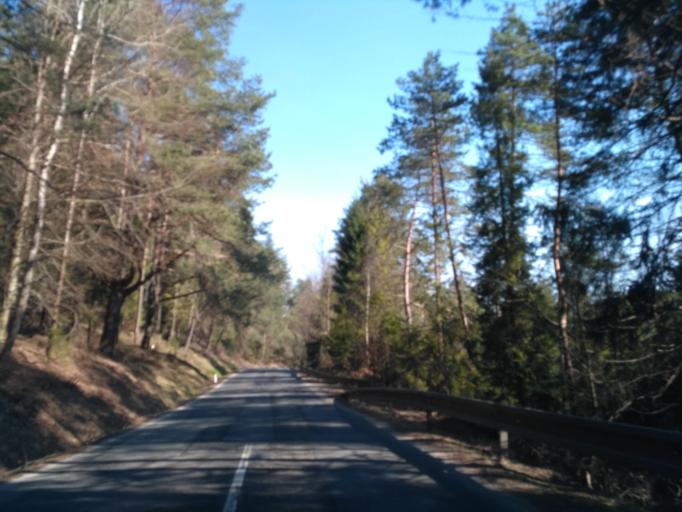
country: SK
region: Kosicky
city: Medzev
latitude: 48.7882
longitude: 20.8021
